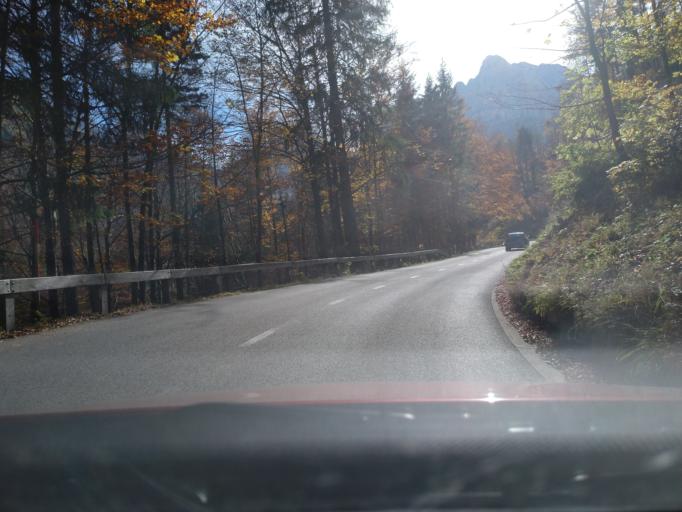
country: SI
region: Kranjska Gora
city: Kranjska Gora
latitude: 46.4602
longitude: 13.7803
